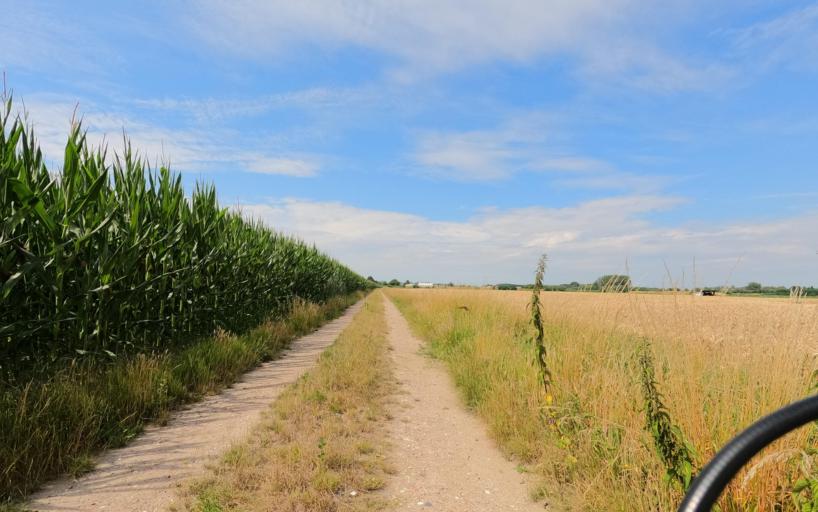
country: BE
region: Flanders
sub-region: Provincie Vlaams-Brabant
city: Kapelle-op-den-Bos
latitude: 51.0042
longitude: 4.3374
